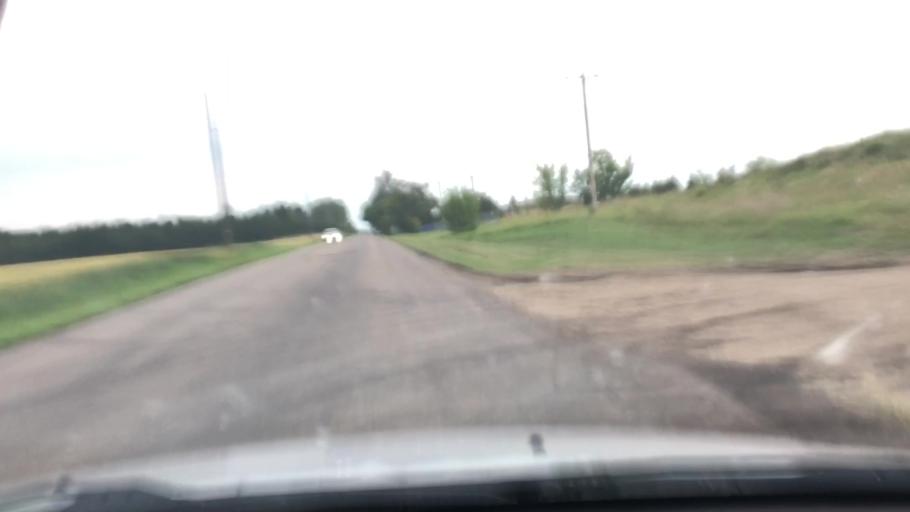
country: CA
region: Alberta
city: Devon
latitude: 53.4215
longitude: -113.6892
